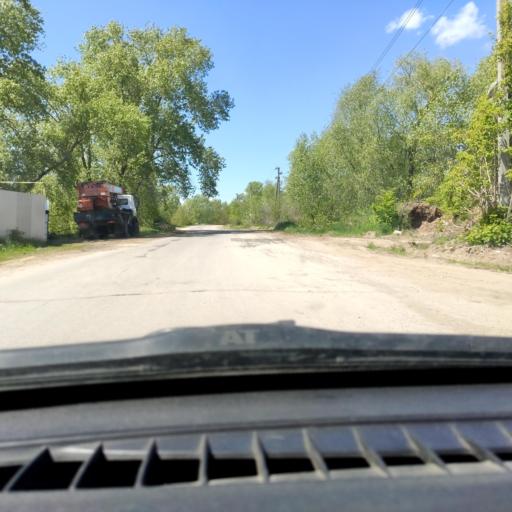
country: RU
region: Samara
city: Zhigulevsk
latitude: 53.4573
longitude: 49.5157
